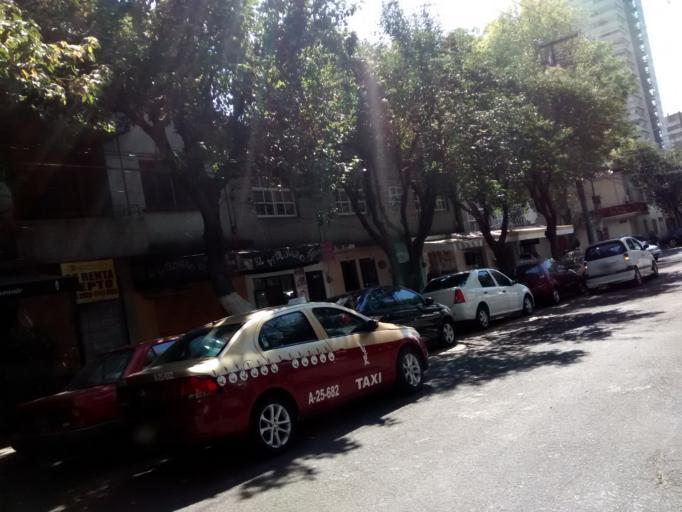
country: MX
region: Mexico City
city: Polanco
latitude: 19.4129
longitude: -99.1800
